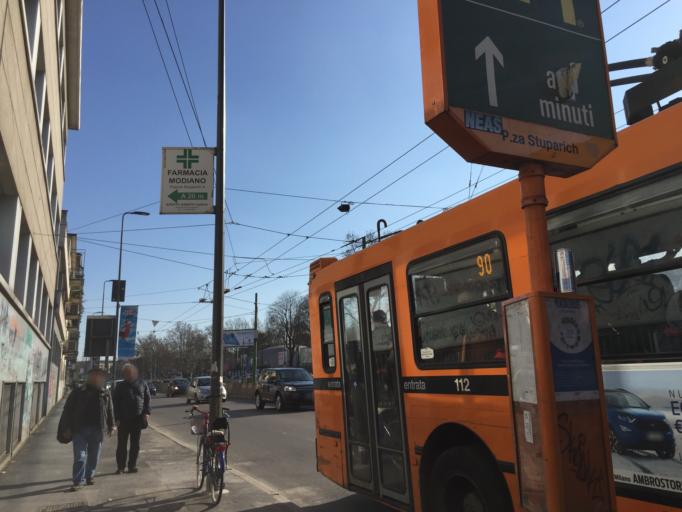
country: IT
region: Lombardy
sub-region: Citta metropolitana di Milano
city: Novate Milanese
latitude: 45.4819
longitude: 9.1433
